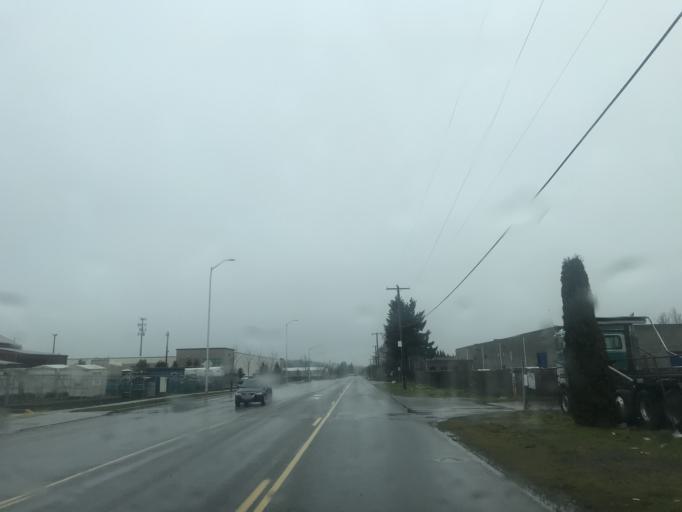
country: US
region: Washington
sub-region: Pierce County
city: Fife
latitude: 47.2137
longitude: -122.3366
